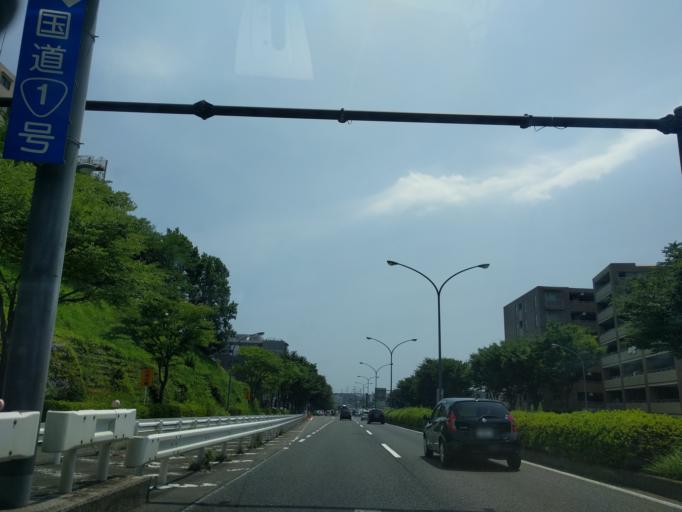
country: JP
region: Kanagawa
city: Yokohama
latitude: 35.4243
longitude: 139.5611
